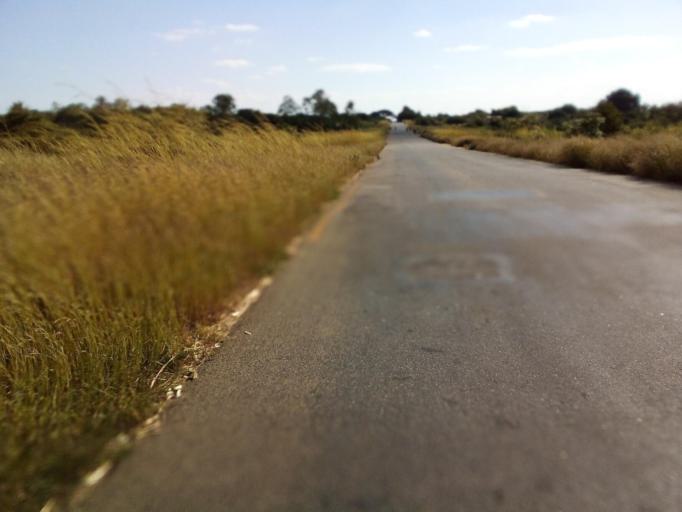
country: MZ
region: Zambezia
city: Quelimane
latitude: -17.5751
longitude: 36.6226
